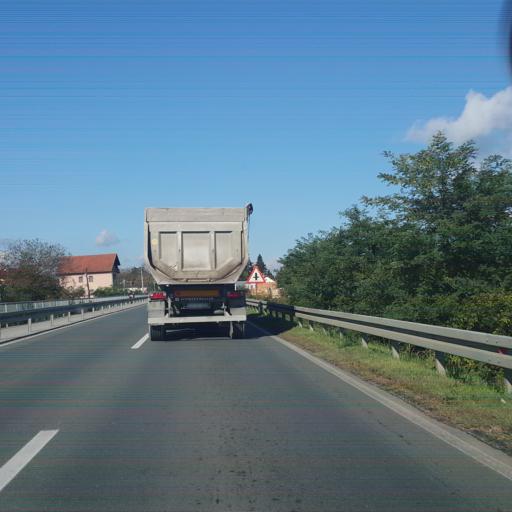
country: RS
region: Central Serbia
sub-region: Raski Okrug
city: Vrnjacka Banja
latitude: 43.6377
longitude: 20.9294
